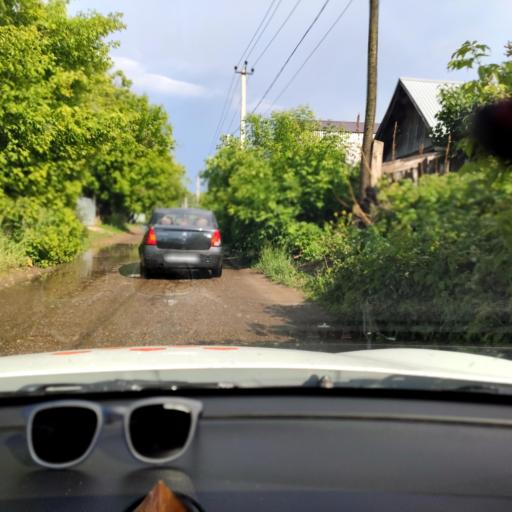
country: RU
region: Tatarstan
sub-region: Zelenodol'skiy Rayon
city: Vasil'yevo
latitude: 55.8277
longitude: 48.7569
